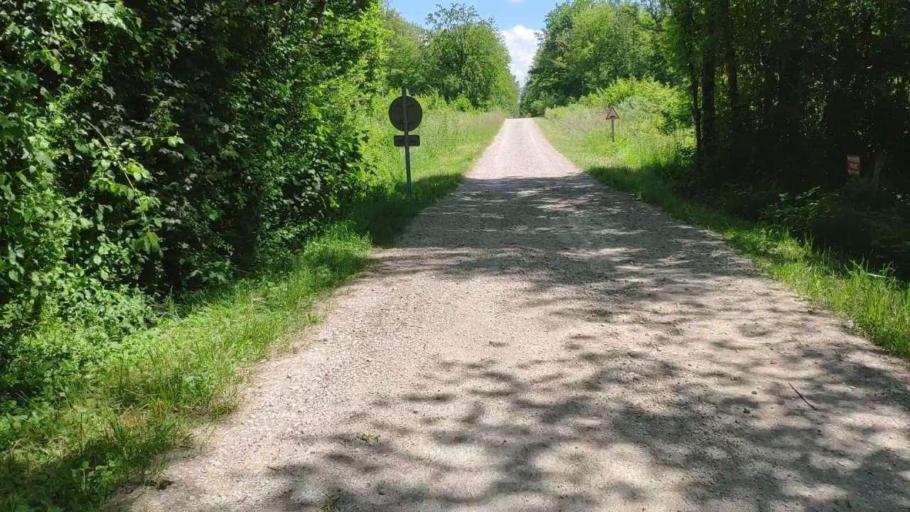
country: FR
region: Franche-Comte
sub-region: Departement du Jura
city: Bletterans
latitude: 46.7826
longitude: 5.4557
